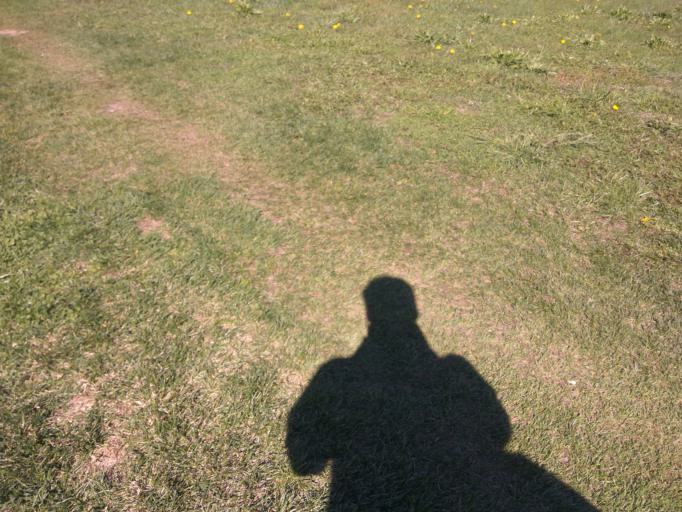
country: RU
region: Moscow
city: Kolomenskoye
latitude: 55.6585
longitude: 37.6698
